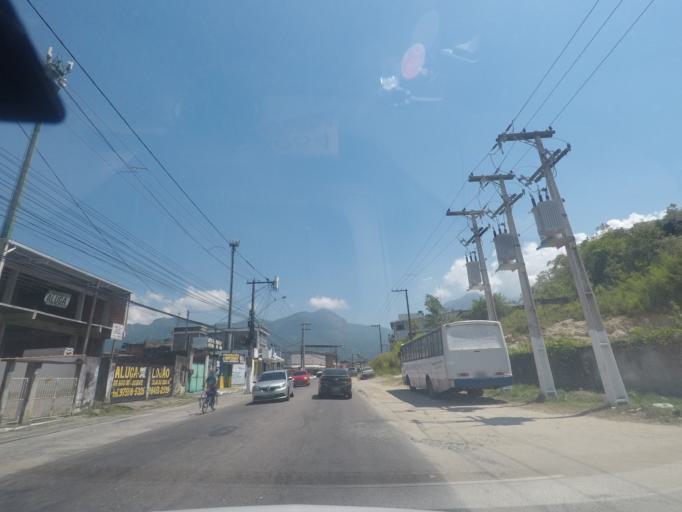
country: BR
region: Rio de Janeiro
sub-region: Petropolis
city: Petropolis
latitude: -22.5961
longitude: -43.1873
